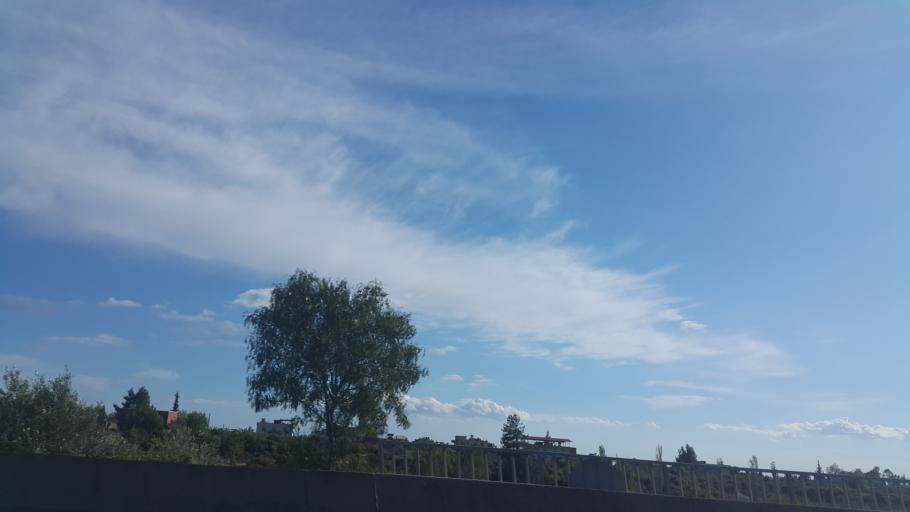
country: TR
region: Adana
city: Yakapinar
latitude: 37.0190
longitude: 35.4938
